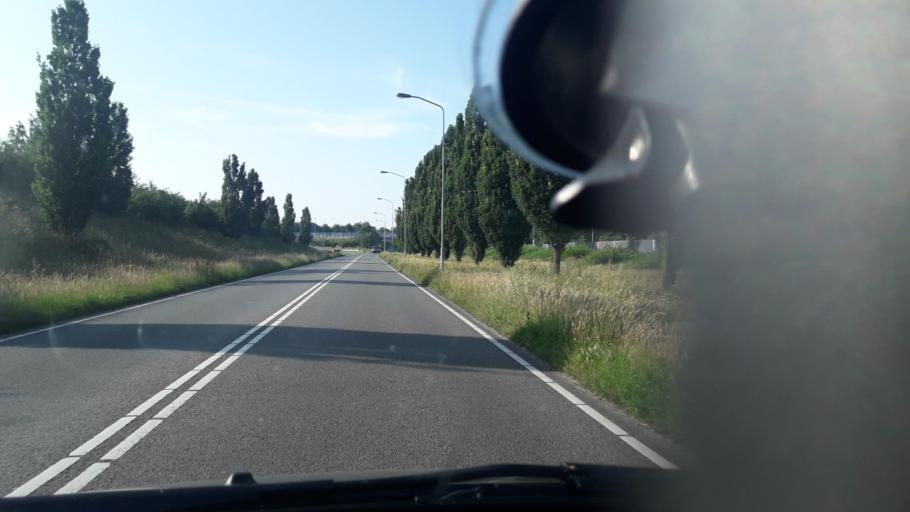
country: NL
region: Gelderland
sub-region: Gemeente Harderwijk
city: Harderwijk
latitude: 52.3274
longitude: 5.6114
